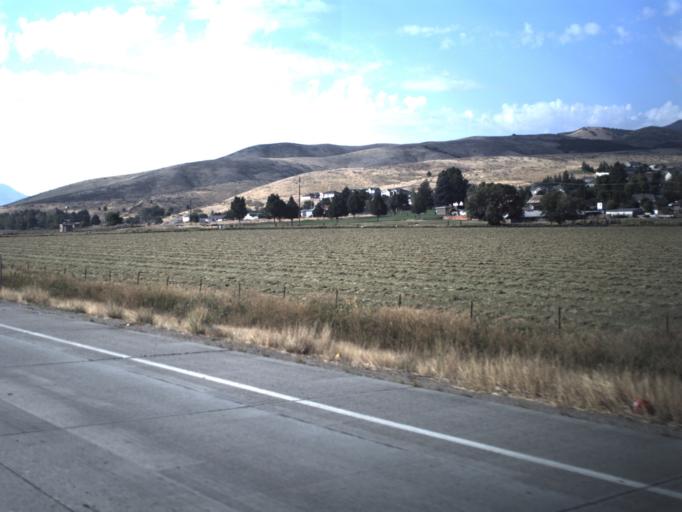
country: US
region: Utah
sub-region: Morgan County
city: Morgan
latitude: 41.0499
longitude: -111.6815
